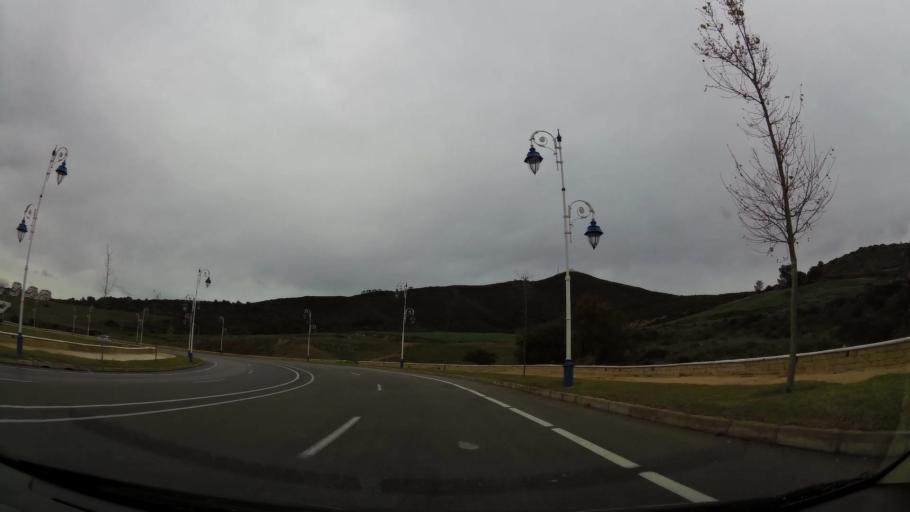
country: MA
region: Tanger-Tetouan
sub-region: Tetouan
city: Martil
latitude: 35.6661
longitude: -5.2980
